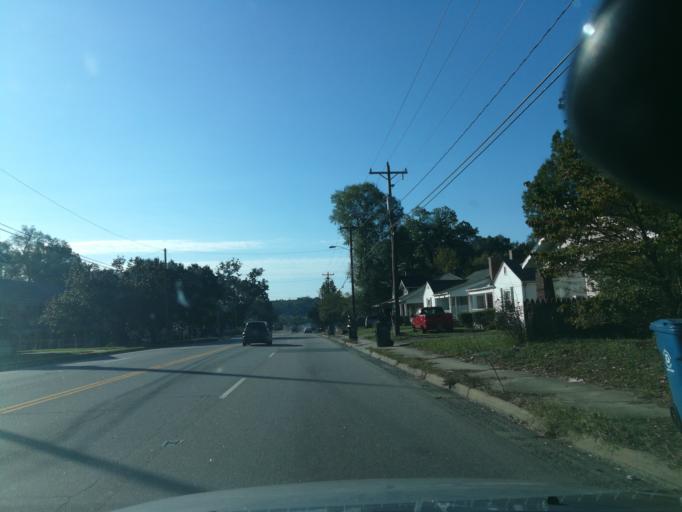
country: US
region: North Carolina
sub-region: Durham County
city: Durham
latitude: 36.0224
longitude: -78.8900
